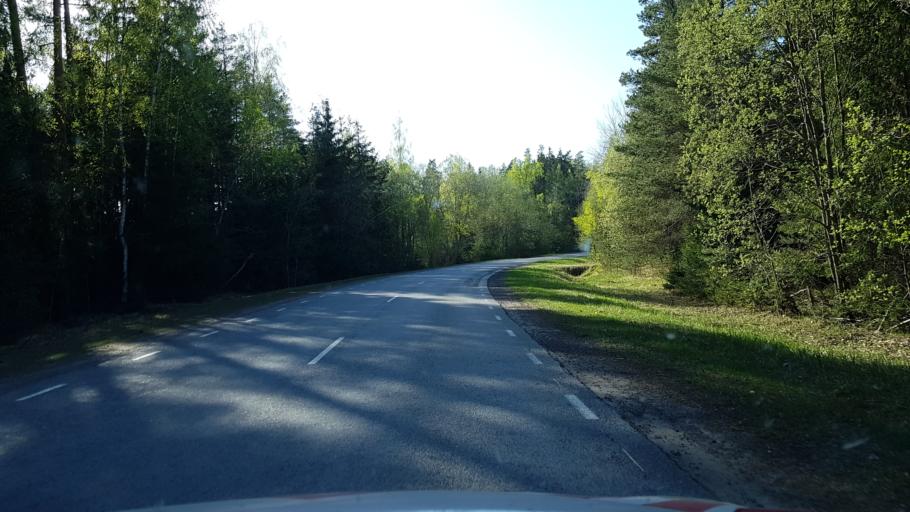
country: EE
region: Paernumaa
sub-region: Paikuse vald
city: Paikuse
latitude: 58.3453
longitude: 24.6723
